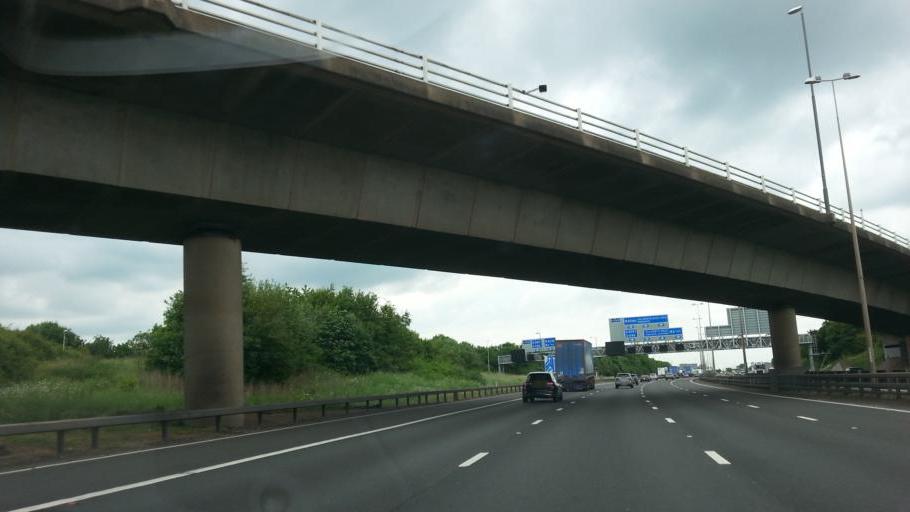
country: GB
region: England
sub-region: Warwickshire
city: Water Orton
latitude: 52.5098
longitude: -1.7258
